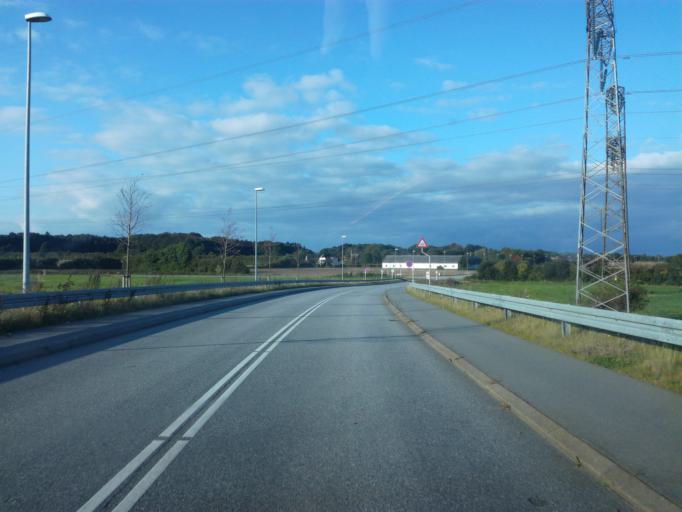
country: DK
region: South Denmark
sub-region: Fredericia Kommune
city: Taulov
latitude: 55.5478
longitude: 9.6250
